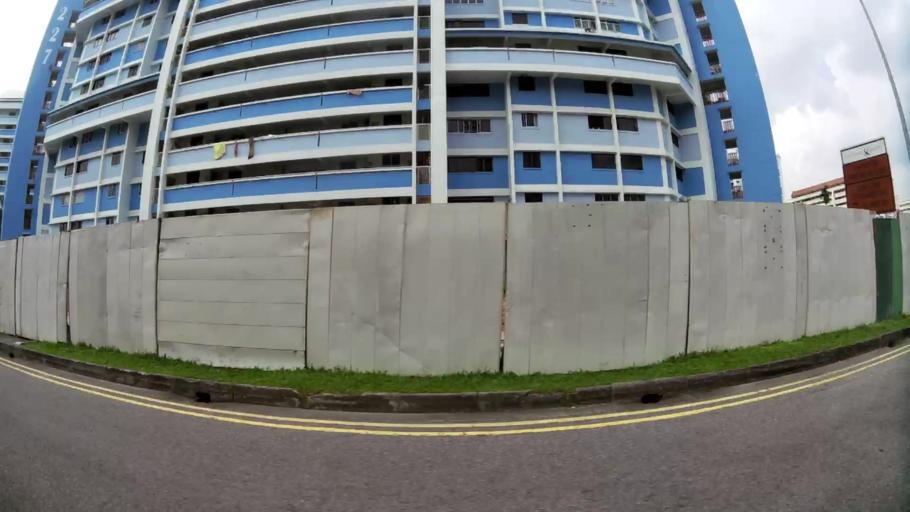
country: SG
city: Singapore
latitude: 1.3553
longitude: 103.9552
